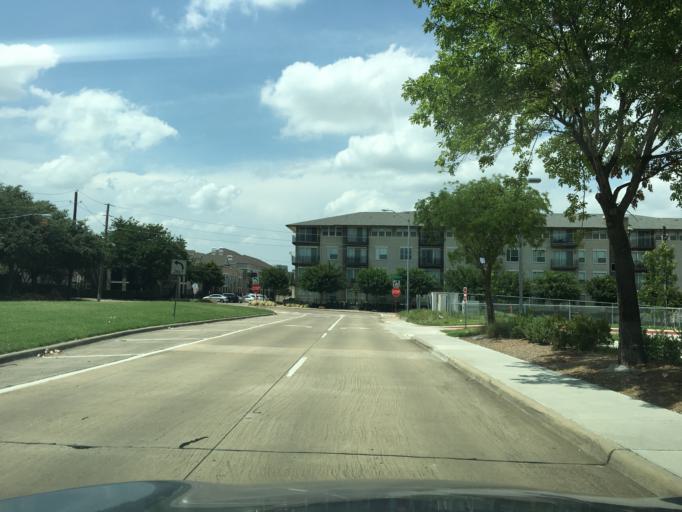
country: US
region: Texas
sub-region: Dallas County
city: Addison
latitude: 32.9480
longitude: -96.8192
